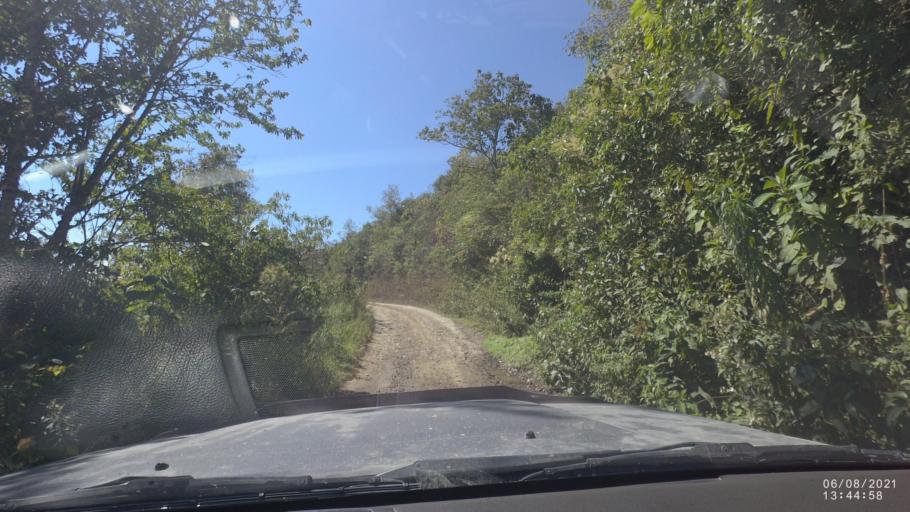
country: BO
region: La Paz
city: Quime
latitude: -16.6738
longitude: -66.7324
